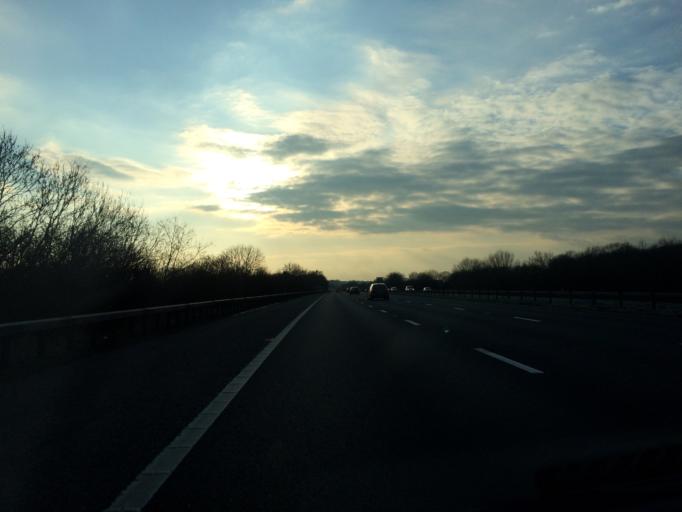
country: GB
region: England
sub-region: Wiltshire
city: Chippenham
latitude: 51.5143
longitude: -2.0999
